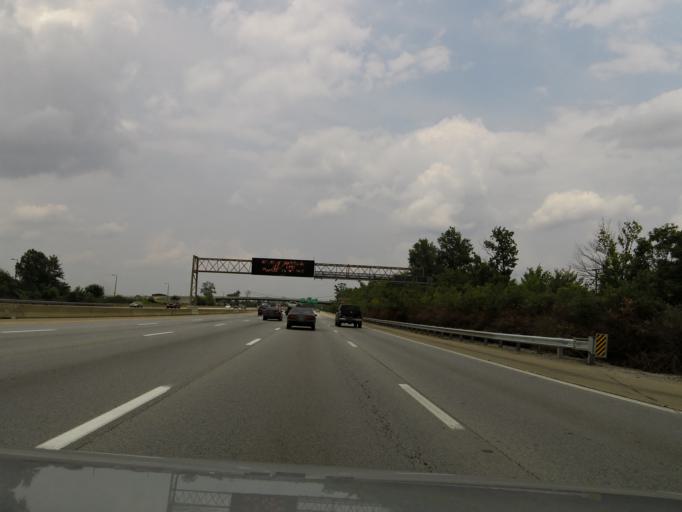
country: US
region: Kentucky
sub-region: Jefferson County
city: Audubon Park
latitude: 38.1651
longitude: -85.7206
